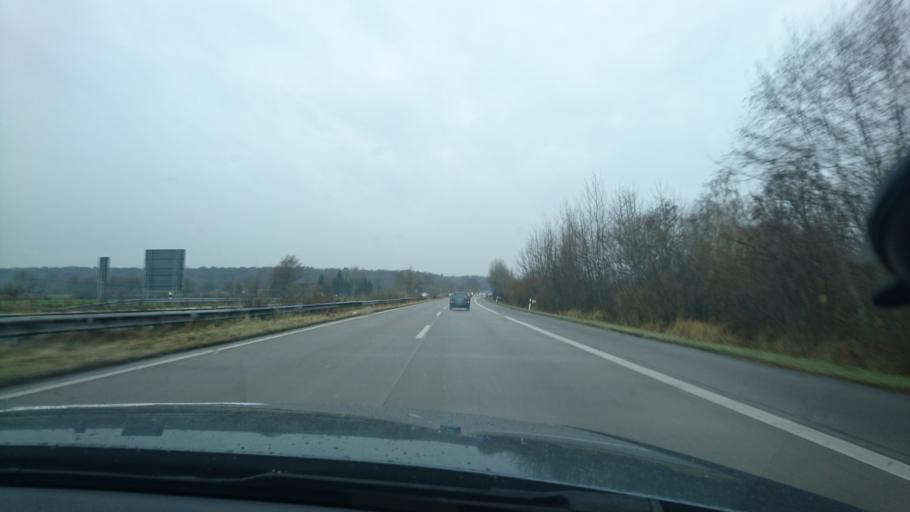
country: DE
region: Schleswig-Holstein
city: Scharbeutz
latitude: 54.0387
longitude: 10.7285
